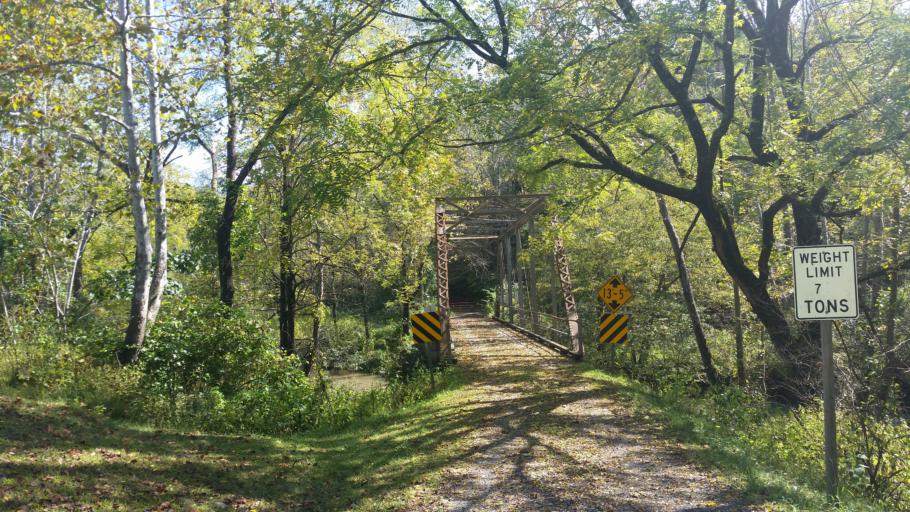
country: US
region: Virginia
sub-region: Franklin County
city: Ferrum
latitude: 36.8937
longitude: -80.1221
